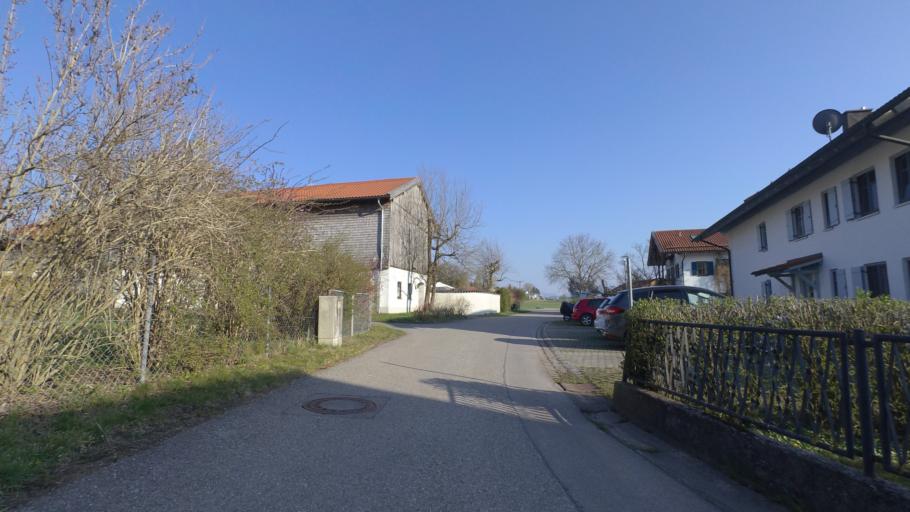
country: DE
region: Bavaria
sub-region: Upper Bavaria
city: Nussdorf
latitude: 47.9077
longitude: 12.5907
